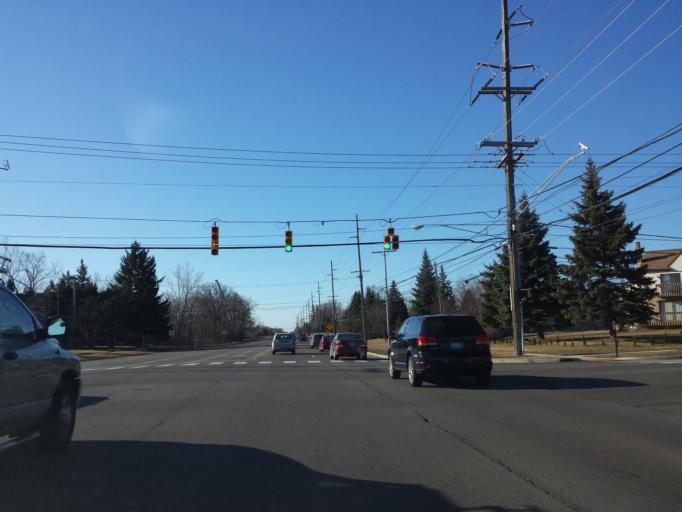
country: US
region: Michigan
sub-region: Oakland County
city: Troy
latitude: 42.5773
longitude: -83.1484
